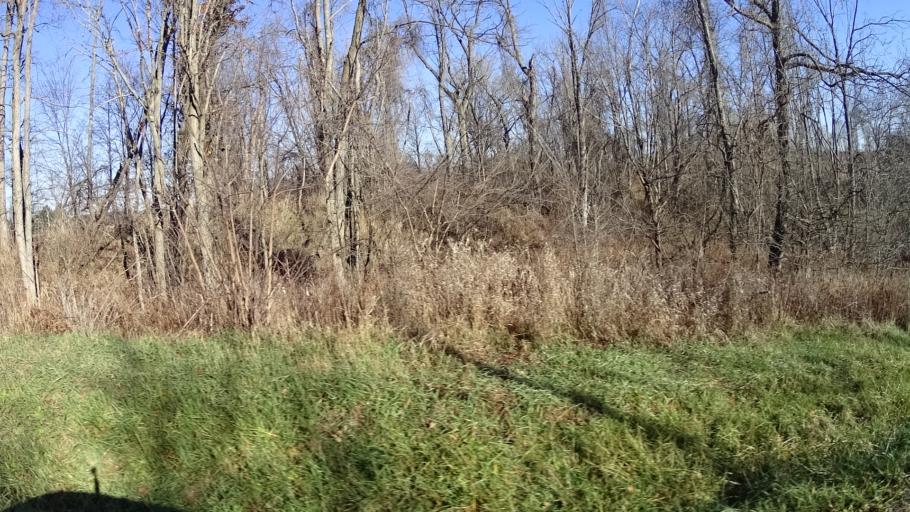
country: US
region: Ohio
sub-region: Lorain County
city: Wellington
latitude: 41.0731
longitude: -82.2782
